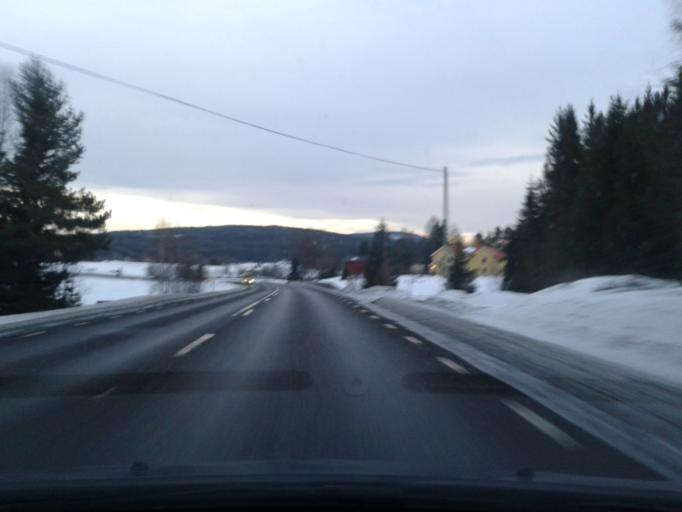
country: SE
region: Vaesternorrland
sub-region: Kramfors Kommun
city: Bollstabruk
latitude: 63.0807
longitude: 17.5388
